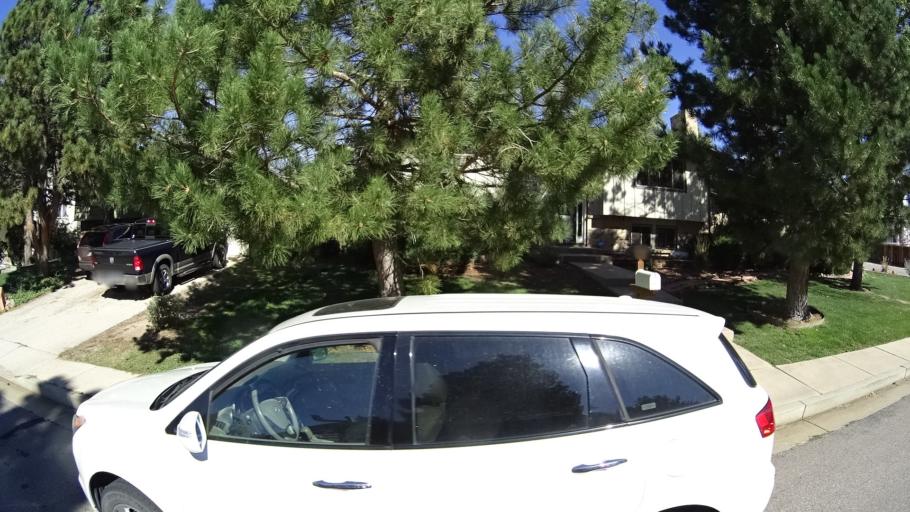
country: US
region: Colorado
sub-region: El Paso County
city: Cimarron Hills
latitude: 38.9181
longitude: -104.7667
